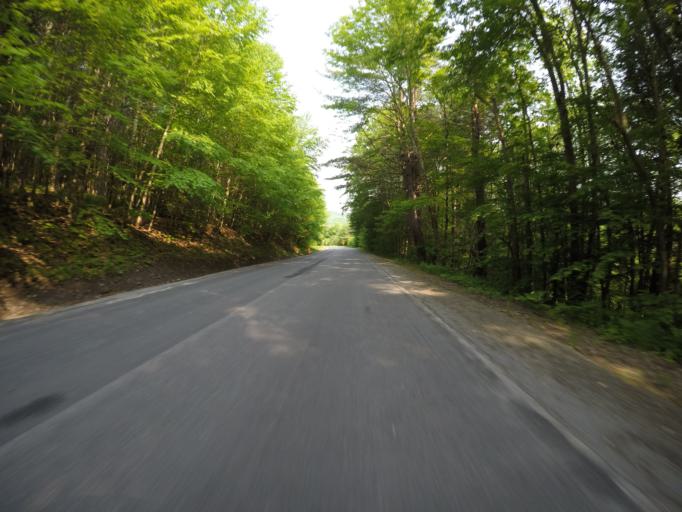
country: US
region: New York
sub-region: Sullivan County
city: Livingston Manor
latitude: 42.1214
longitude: -74.6864
